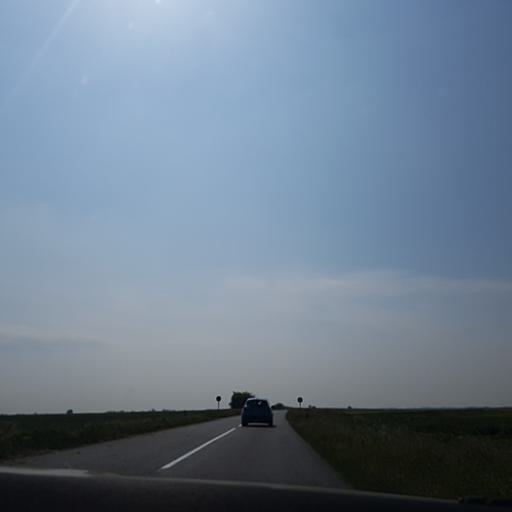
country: RS
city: Jarkovac
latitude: 45.3119
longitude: 20.7502
